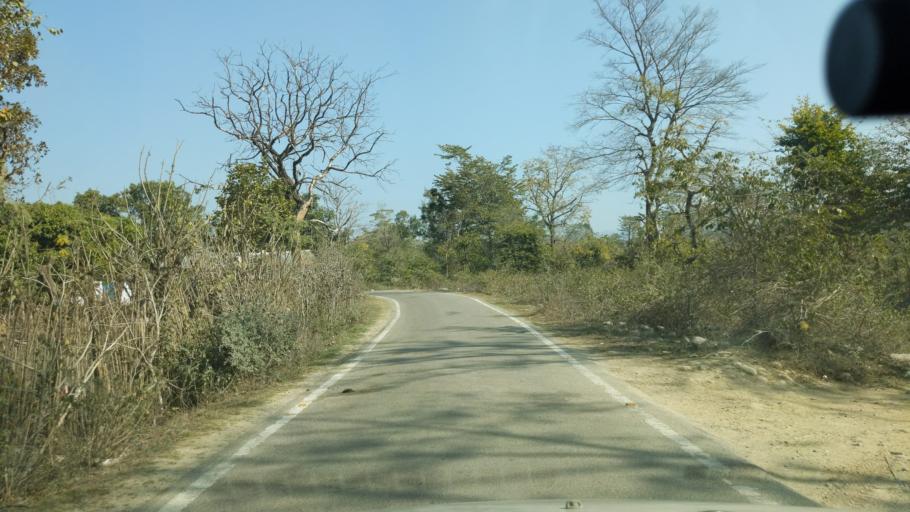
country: IN
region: Uttarakhand
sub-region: Naini Tal
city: Ramnagar
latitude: 29.4190
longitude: 79.1382
